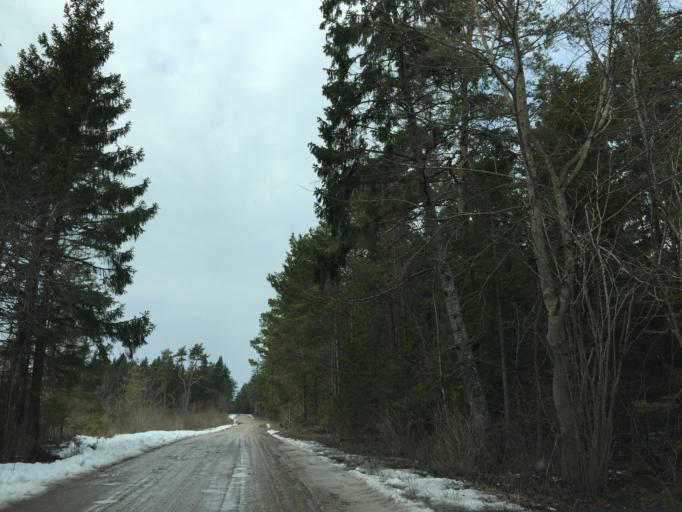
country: EE
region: Saare
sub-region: Kuressaare linn
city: Kuressaare
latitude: 58.4257
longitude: 22.1509
